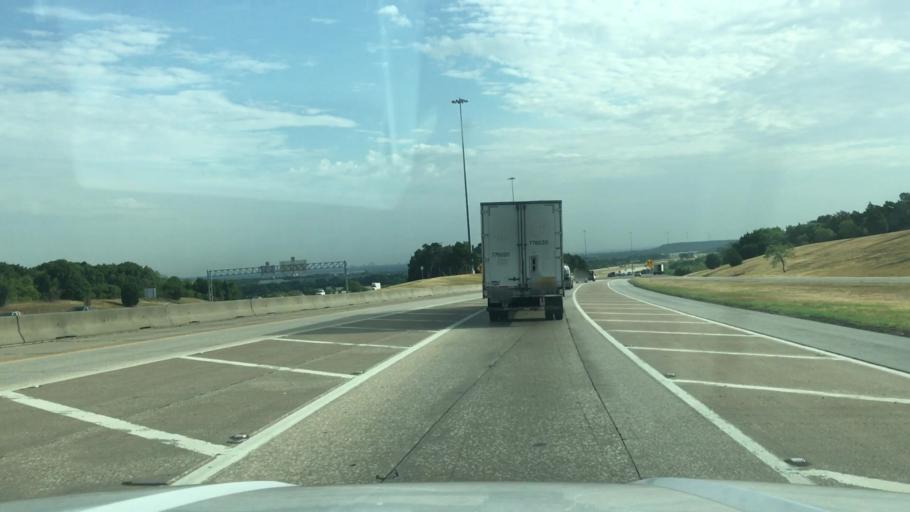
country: US
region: Texas
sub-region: Dallas County
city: Duncanville
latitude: 32.6762
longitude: -96.9461
